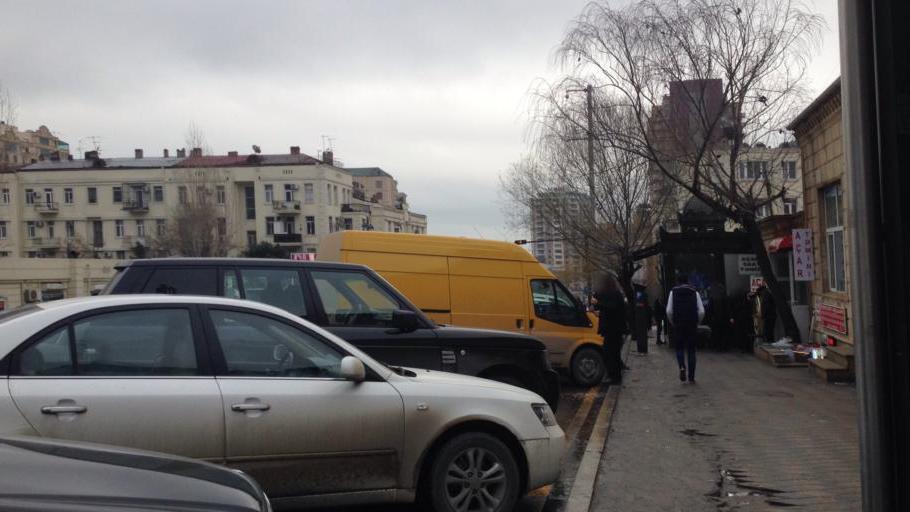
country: AZ
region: Baki
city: Baku
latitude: 40.3814
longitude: 49.8389
